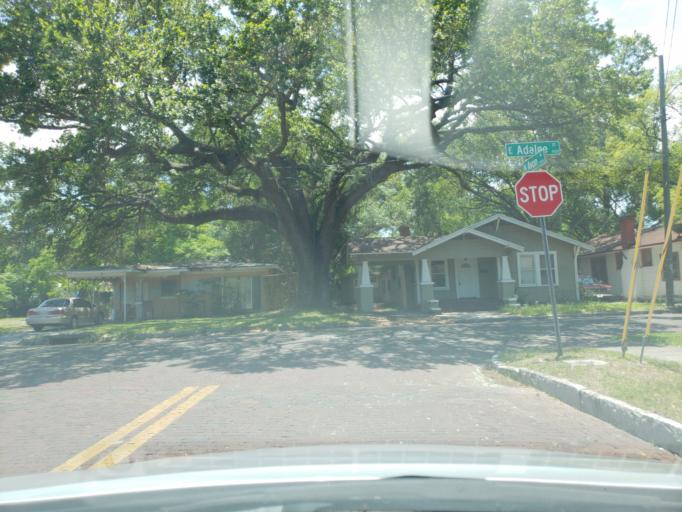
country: US
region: Florida
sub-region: Hillsborough County
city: Tampa
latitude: 27.9726
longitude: -82.4561
